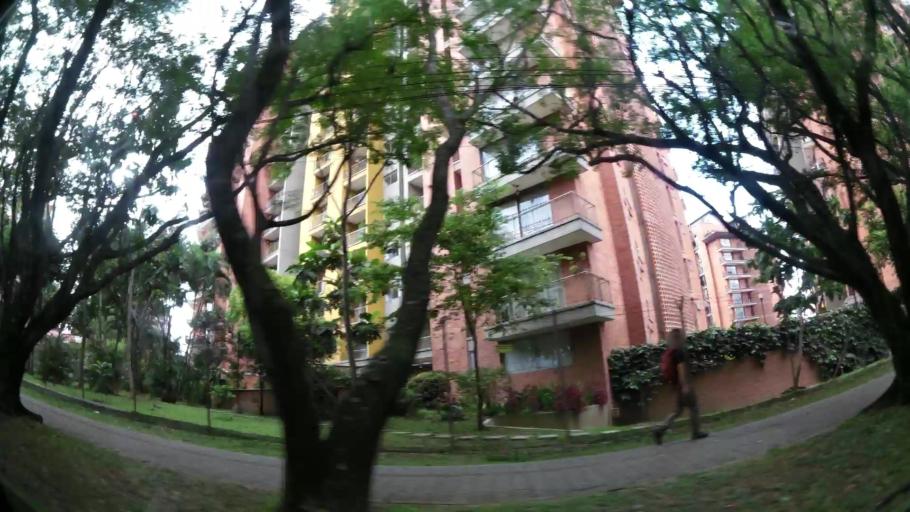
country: CO
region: Antioquia
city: Envigado
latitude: 6.1800
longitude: -75.5832
